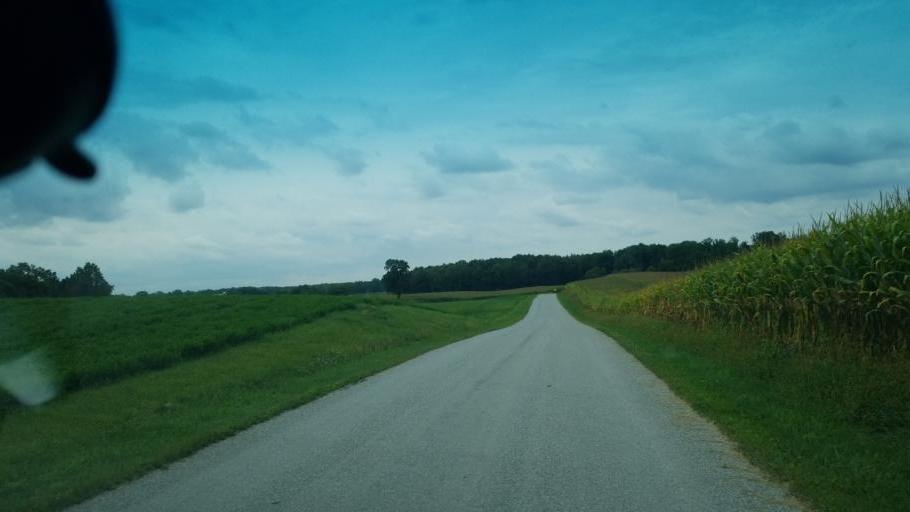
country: US
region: Ohio
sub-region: Richland County
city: Shelby
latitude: 40.9359
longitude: -82.5980
